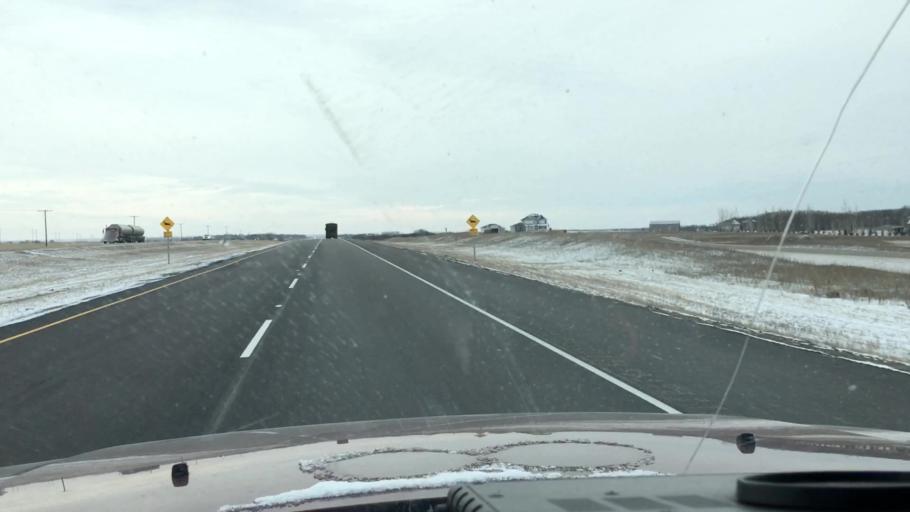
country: CA
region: Saskatchewan
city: Saskatoon
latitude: 51.9311
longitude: -106.5358
